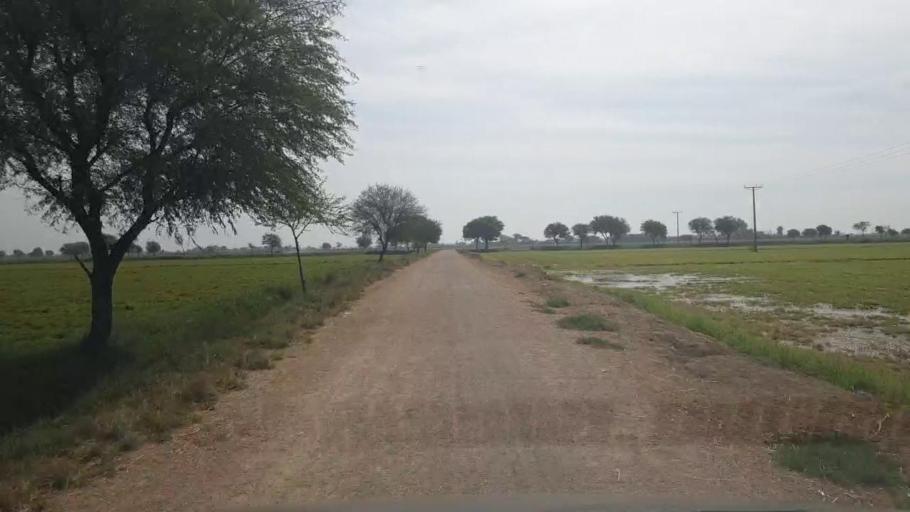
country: PK
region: Sindh
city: Umarkot
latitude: 25.3576
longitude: 69.6040
